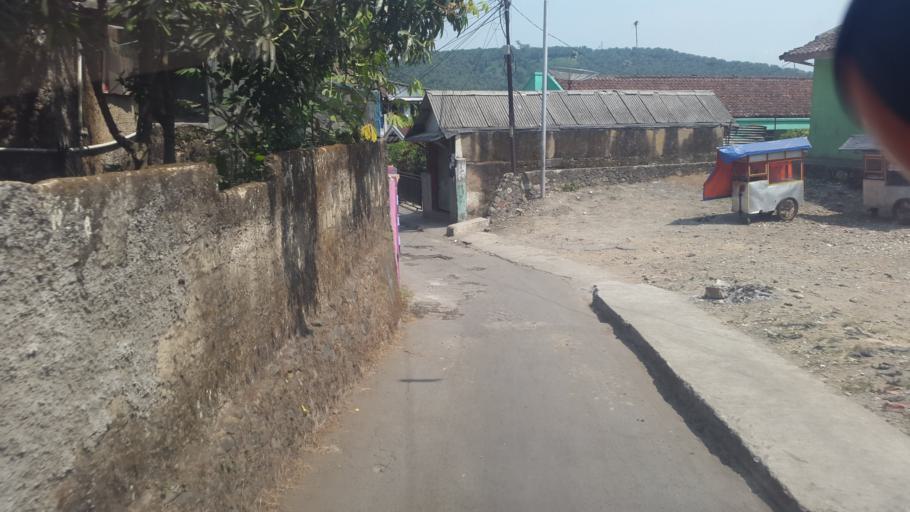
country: ID
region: West Java
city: Cicurug
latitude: -6.8874
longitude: 106.7786
